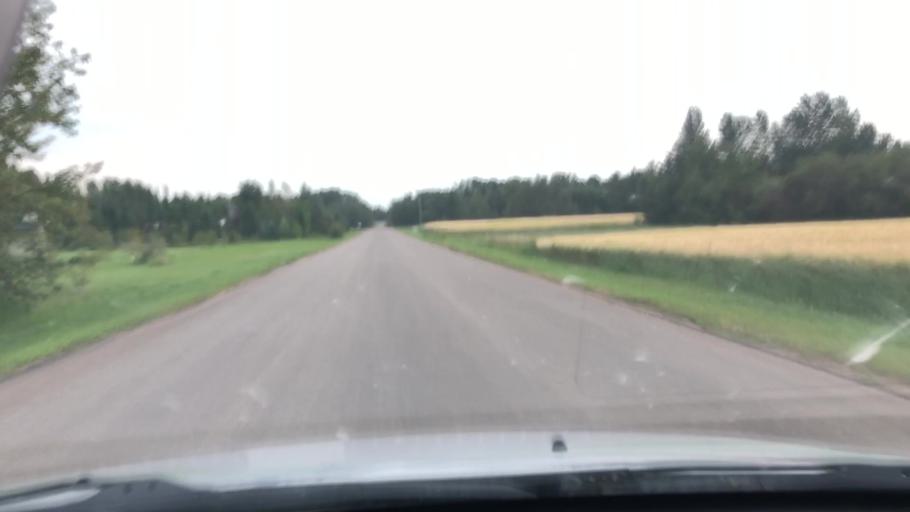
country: CA
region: Alberta
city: Devon
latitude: 53.4311
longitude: -113.6769
